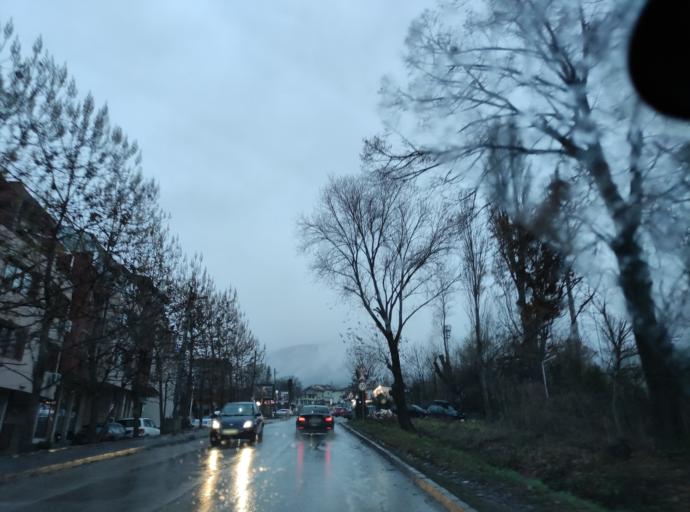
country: BG
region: Sofia-Capital
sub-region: Stolichna Obshtina
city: Sofia
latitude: 42.6367
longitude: 23.3108
